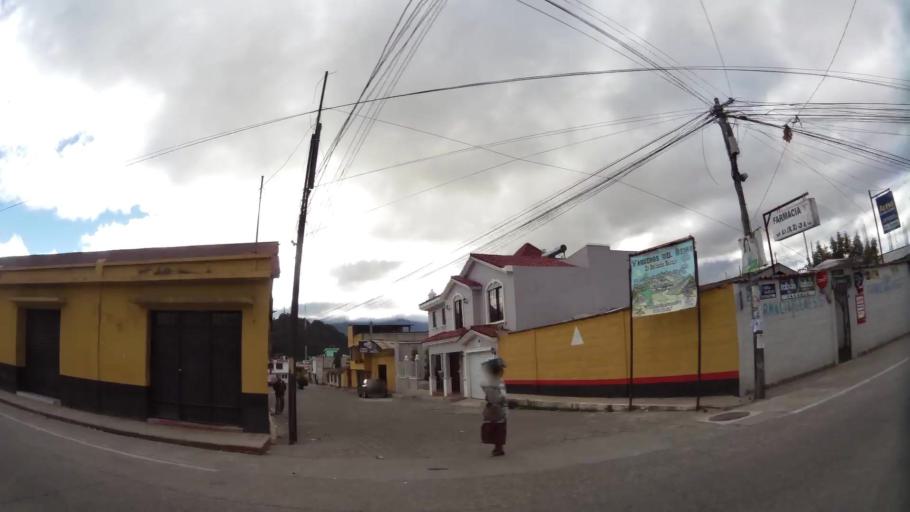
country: GT
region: Quetzaltenango
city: Salcaja
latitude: 14.8761
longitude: -91.4621
